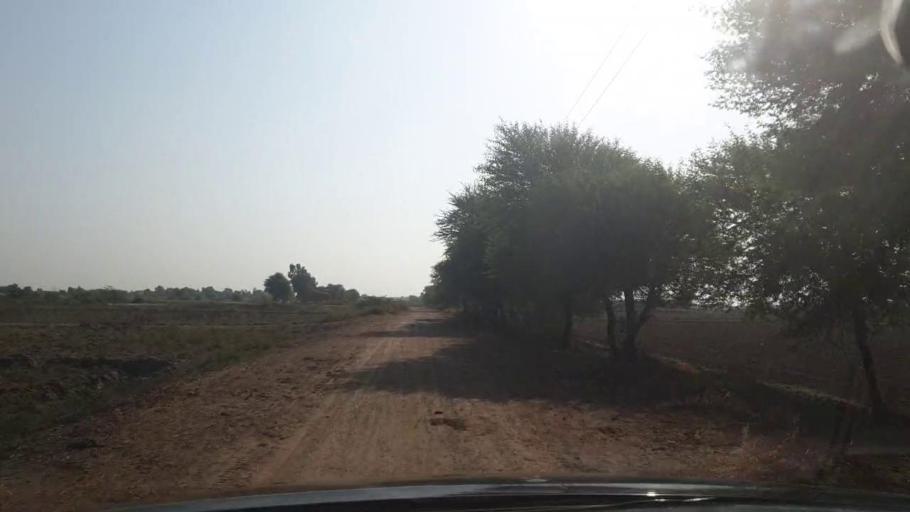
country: PK
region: Sindh
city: Tando Bago
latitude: 24.6510
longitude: 69.1551
